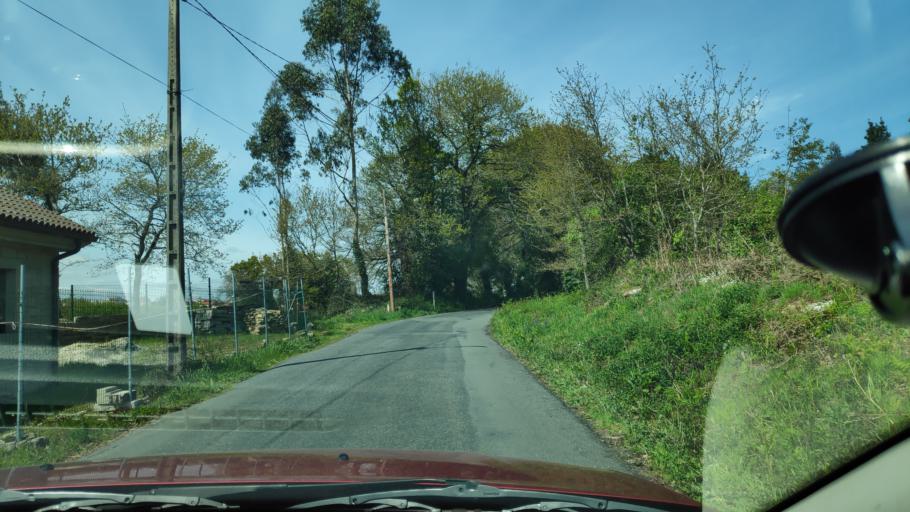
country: ES
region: Galicia
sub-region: Provincia da Coruna
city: Santiago de Compostela
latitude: 42.8952
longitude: -8.5224
